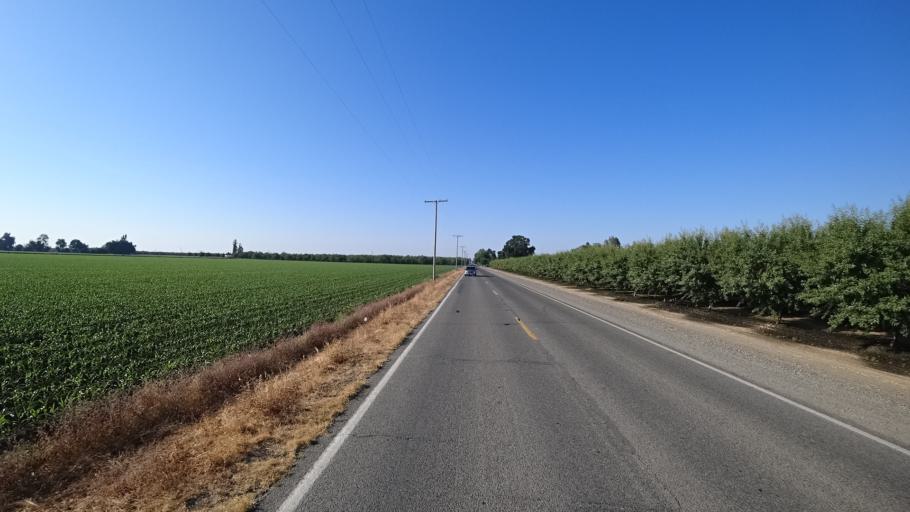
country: US
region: California
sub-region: Kings County
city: Armona
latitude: 36.2871
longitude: -119.7091
